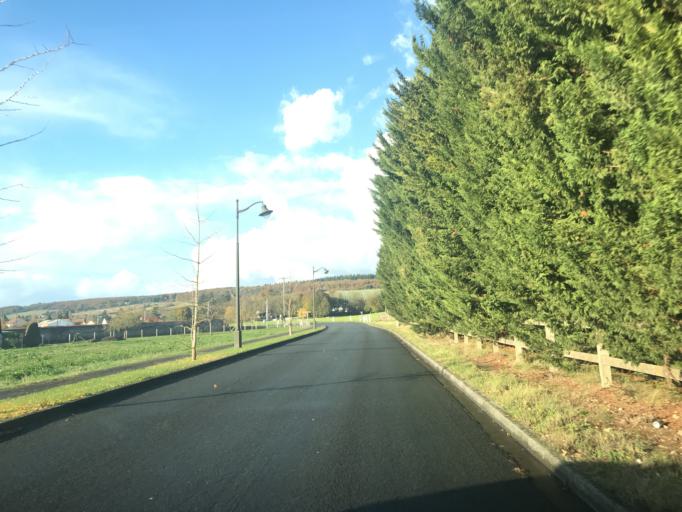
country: FR
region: Haute-Normandie
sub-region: Departement de l'Eure
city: Saint-Aubin-sur-Gaillon
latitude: 49.0917
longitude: 1.2864
